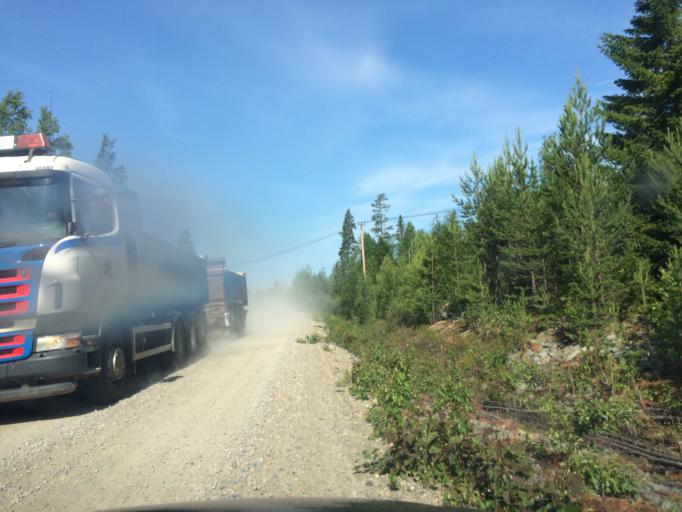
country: SE
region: Vaesternorrland
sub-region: Kramfors Kommun
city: Bollstabruk
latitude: 63.1718
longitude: 17.8164
